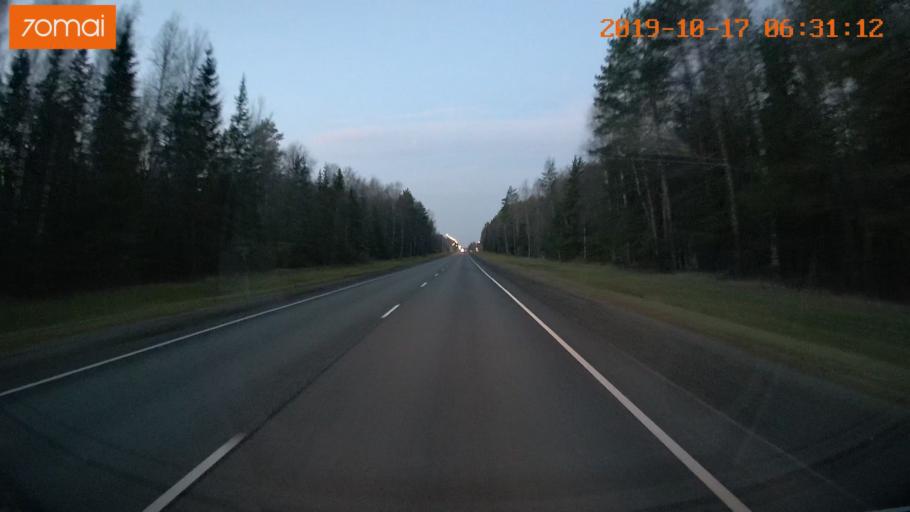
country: RU
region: Ivanovo
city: Lezhnevo
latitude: 56.7297
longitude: 40.7029
